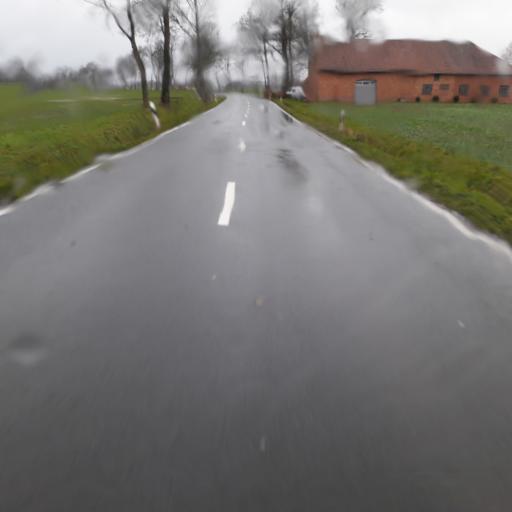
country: DE
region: Lower Saxony
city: Raddestorf
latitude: 52.4177
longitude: 8.9633
